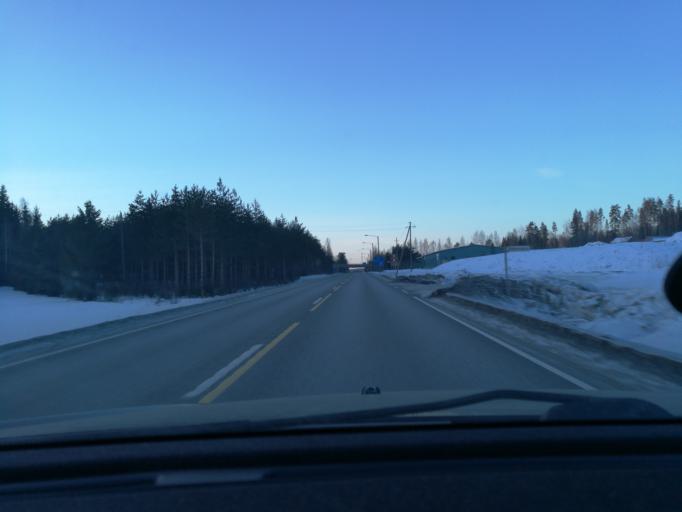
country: FI
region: Uusimaa
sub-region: Helsinki
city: Vihti
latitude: 60.4061
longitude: 24.4552
